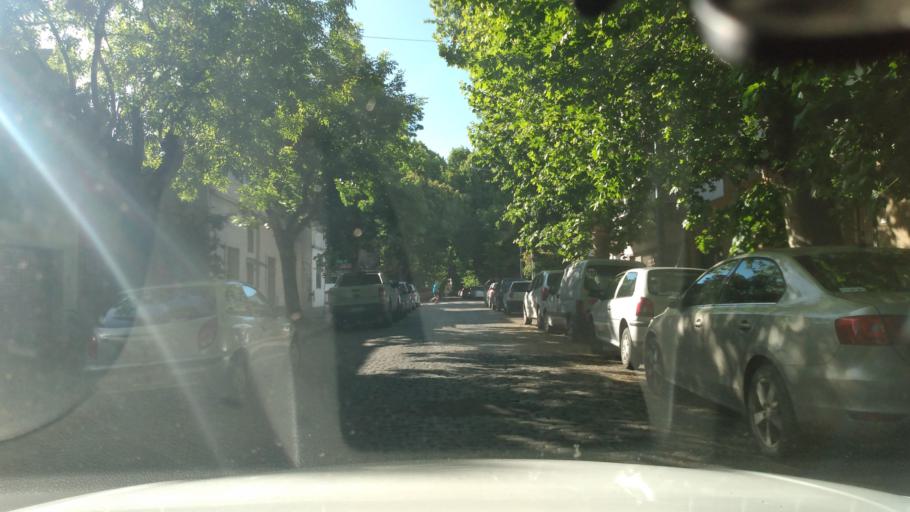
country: AR
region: Buenos Aires F.D.
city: Villa Santa Rita
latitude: -34.5810
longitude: -58.4863
